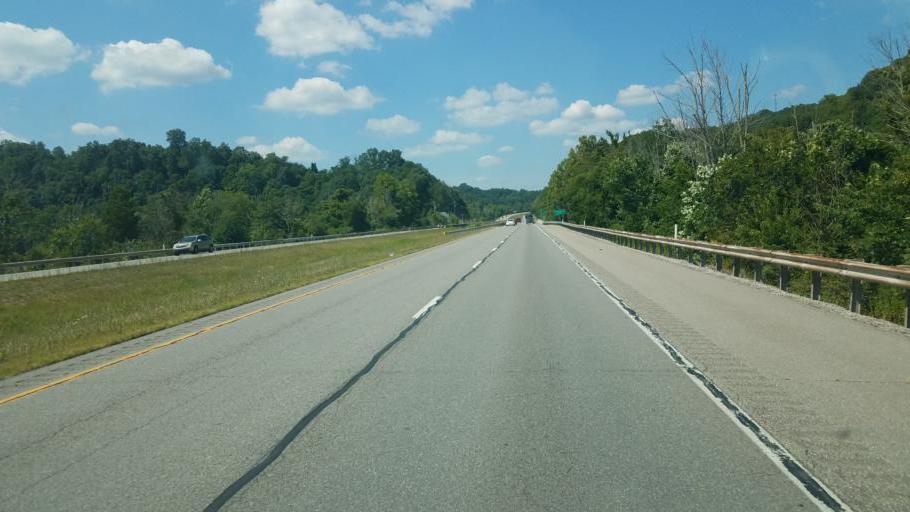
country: US
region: West Virginia
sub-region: Kanawha County
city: Sissonville
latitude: 38.5241
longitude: -81.6440
